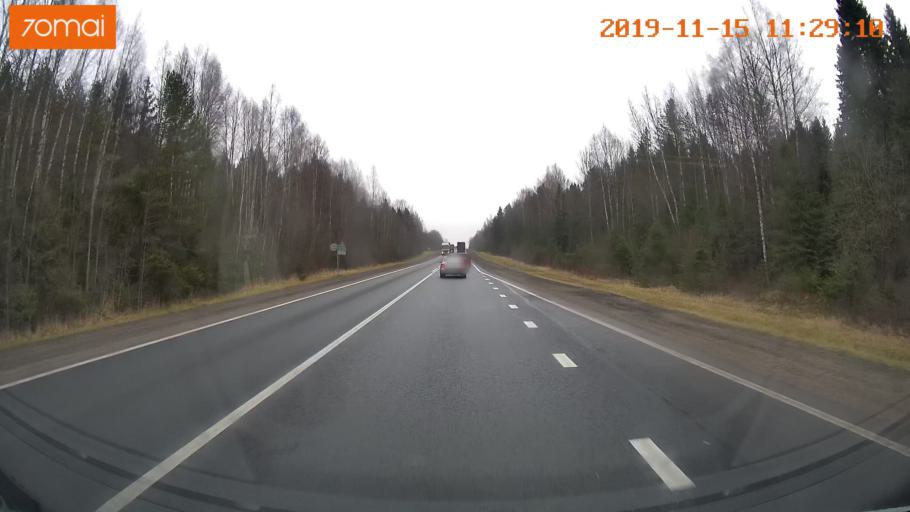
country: RU
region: Vologda
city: Molochnoye
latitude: 59.1746
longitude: 39.5047
